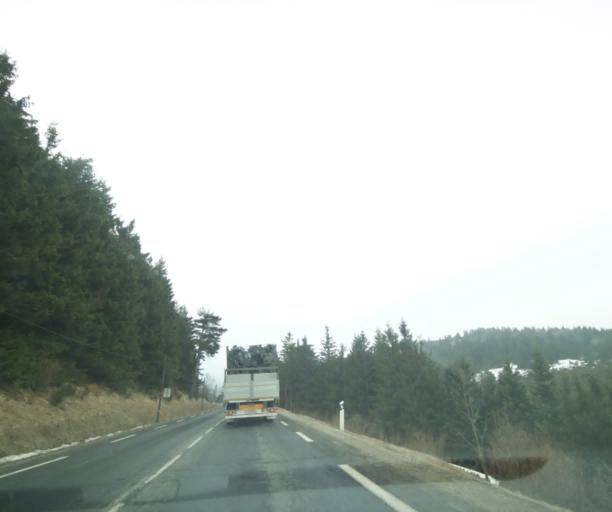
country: FR
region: Languedoc-Roussillon
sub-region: Departement de la Lozere
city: Langogne
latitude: 44.7148
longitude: 4.0075
